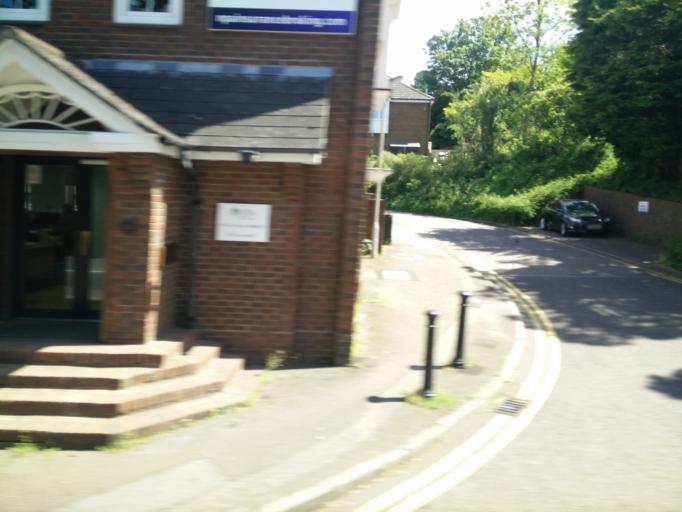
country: GB
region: England
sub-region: Hertfordshire
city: Hitchin
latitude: 51.9446
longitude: -0.2771
